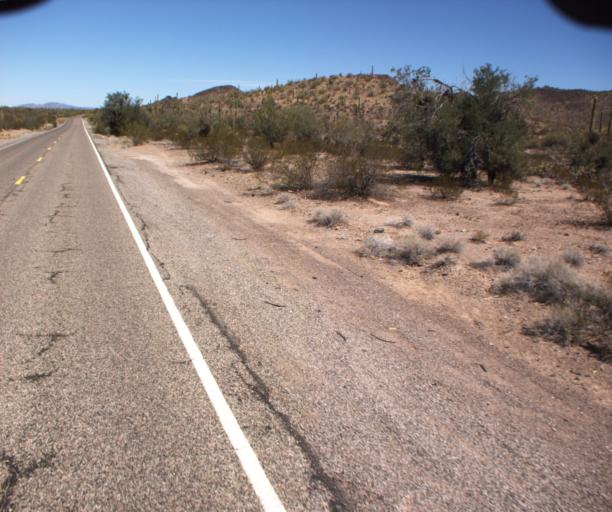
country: US
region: Arizona
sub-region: Pima County
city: Ajo
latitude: 32.2130
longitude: -112.7579
